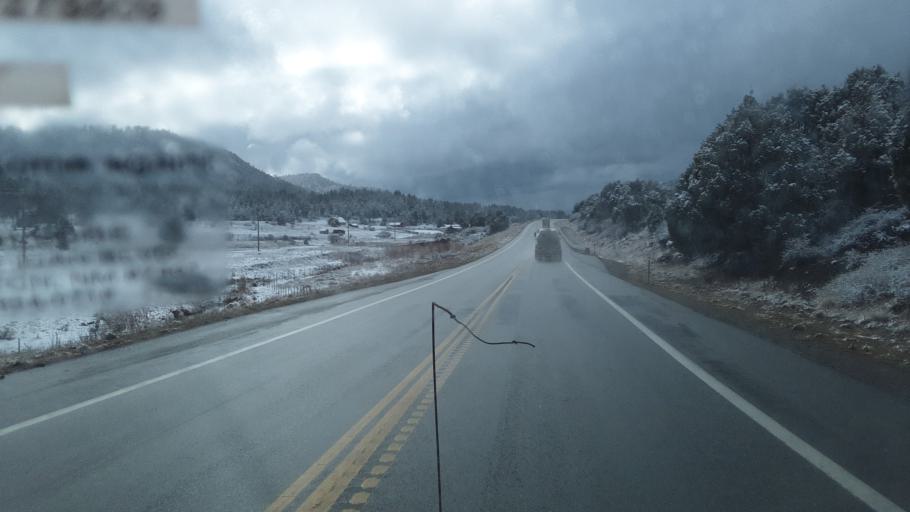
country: US
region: Colorado
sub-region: Archuleta County
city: Pagosa Springs
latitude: 37.2305
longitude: -107.1885
